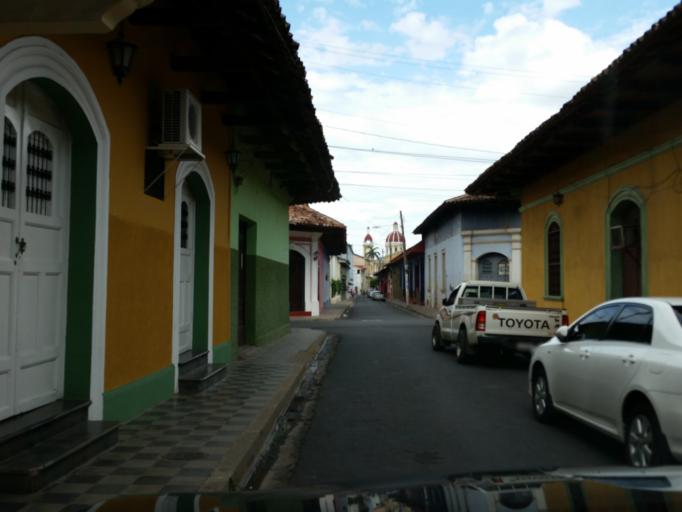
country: NI
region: Granada
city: Granada
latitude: 11.9300
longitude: -85.9568
